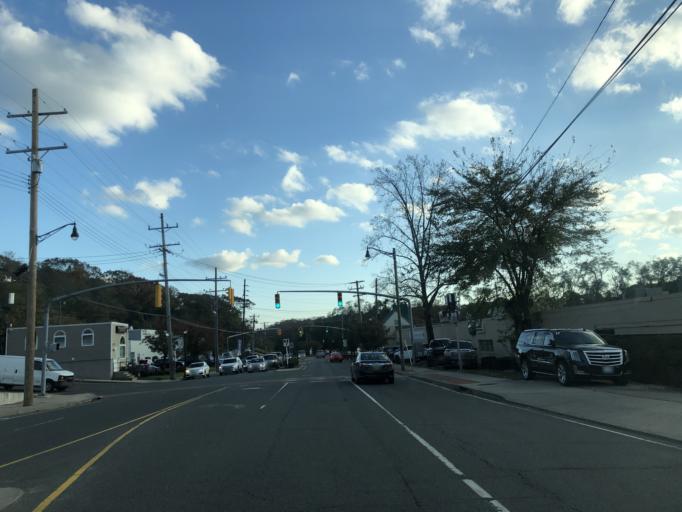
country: US
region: New York
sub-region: Nassau County
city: Glen Cove
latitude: 40.8536
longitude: -73.6195
